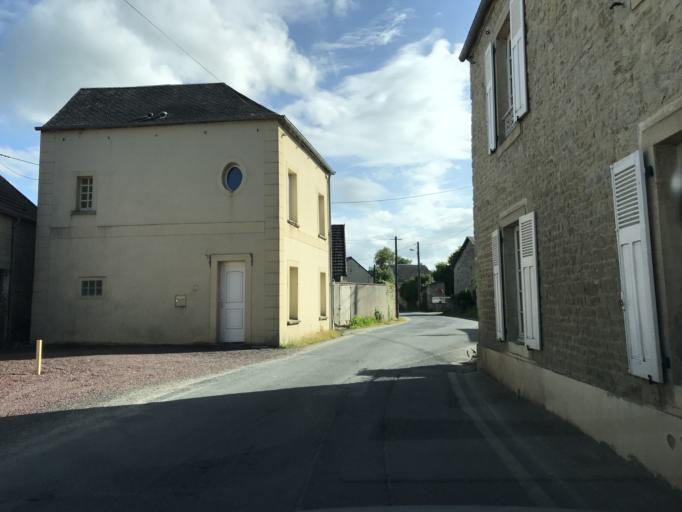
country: FR
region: Lower Normandy
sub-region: Departement du Calvados
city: Grandcamp-Maisy
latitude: 49.3423
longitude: -1.0077
